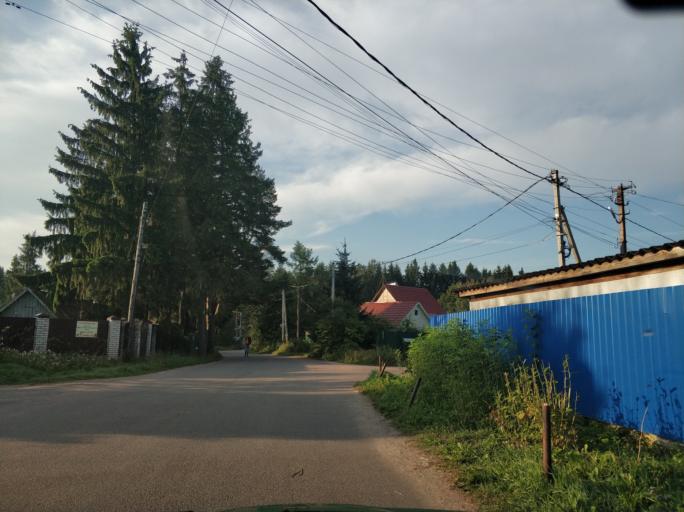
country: RU
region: Leningrad
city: Shcheglovo
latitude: 60.0528
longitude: 30.7446
